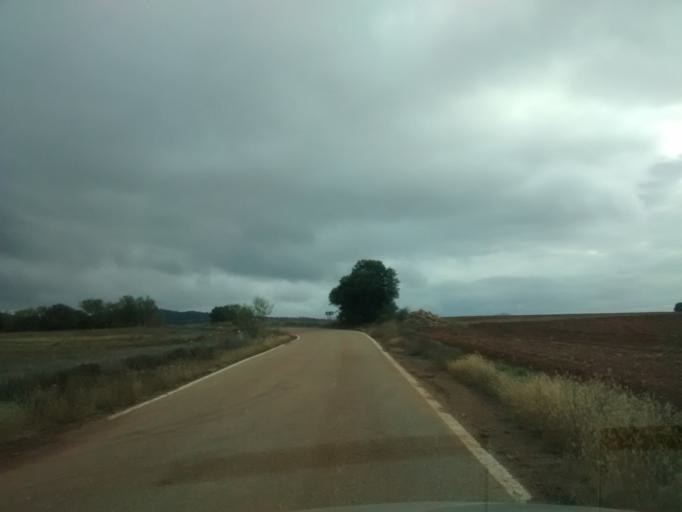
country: ES
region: Aragon
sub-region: Provincia de Zaragoza
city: Gallocanta
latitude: 40.9919
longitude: -1.4928
